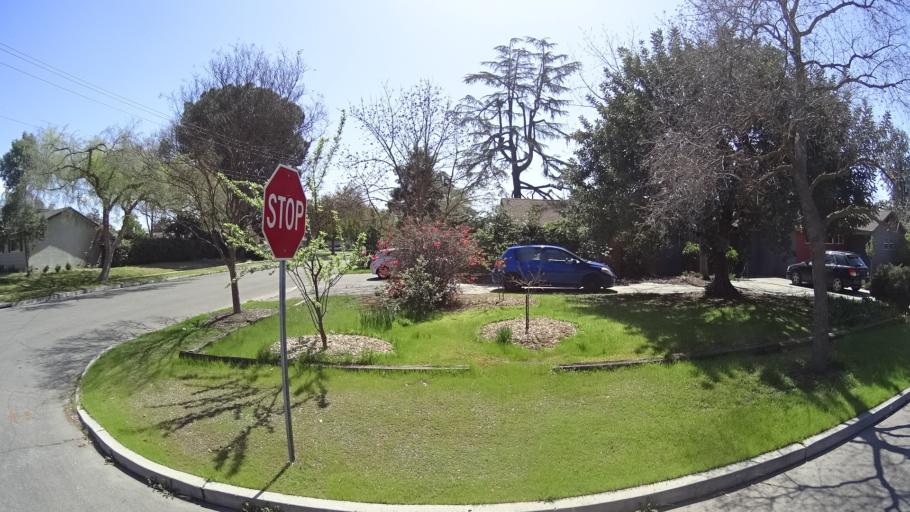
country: US
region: California
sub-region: Fresno County
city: Fresno
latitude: 36.8056
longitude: -119.8221
